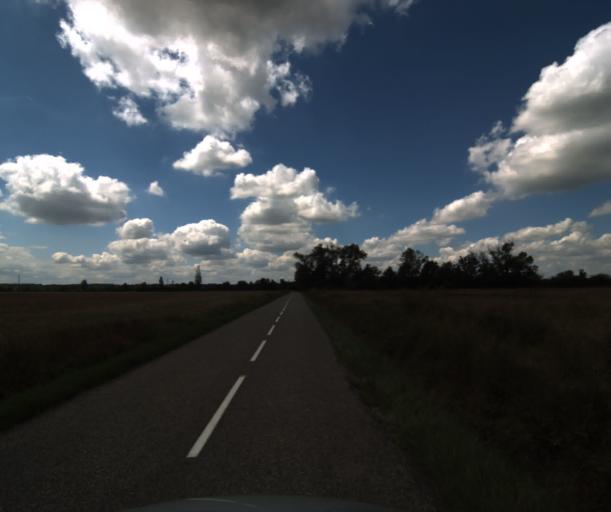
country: FR
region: Midi-Pyrenees
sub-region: Departement de la Haute-Garonne
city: Lherm
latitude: 43.4266
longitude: 1.2480
